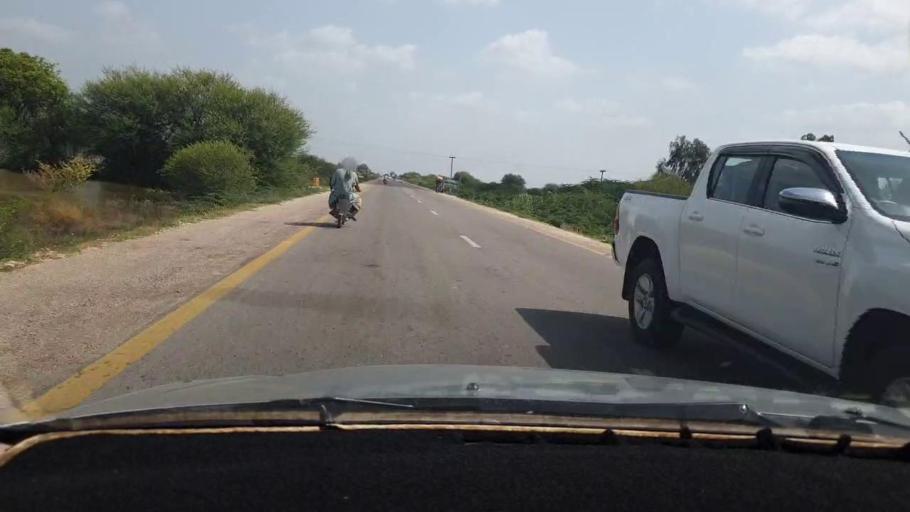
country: PK
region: Sindh
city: Digri
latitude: 25.1089
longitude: 69.1634
